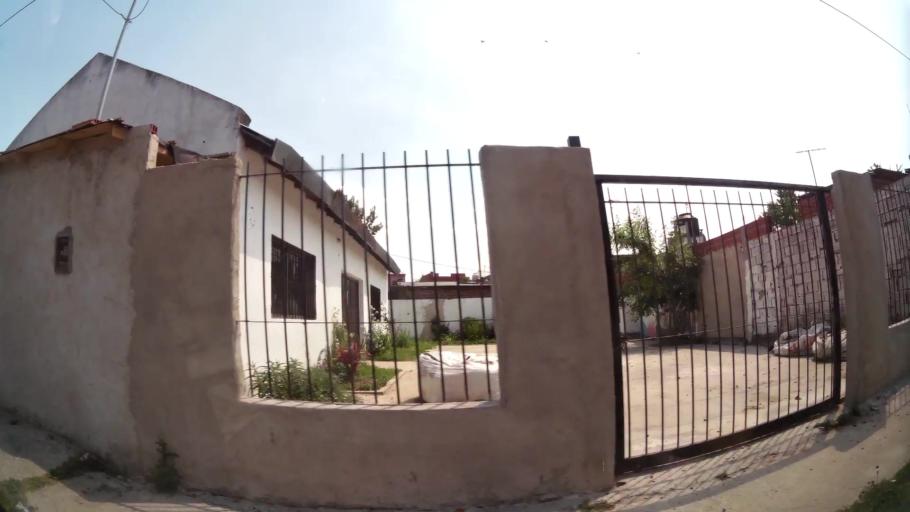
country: AR
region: Buenos Aires
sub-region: Partido de Tigre
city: Tigre
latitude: -34.4676
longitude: -58.5929
